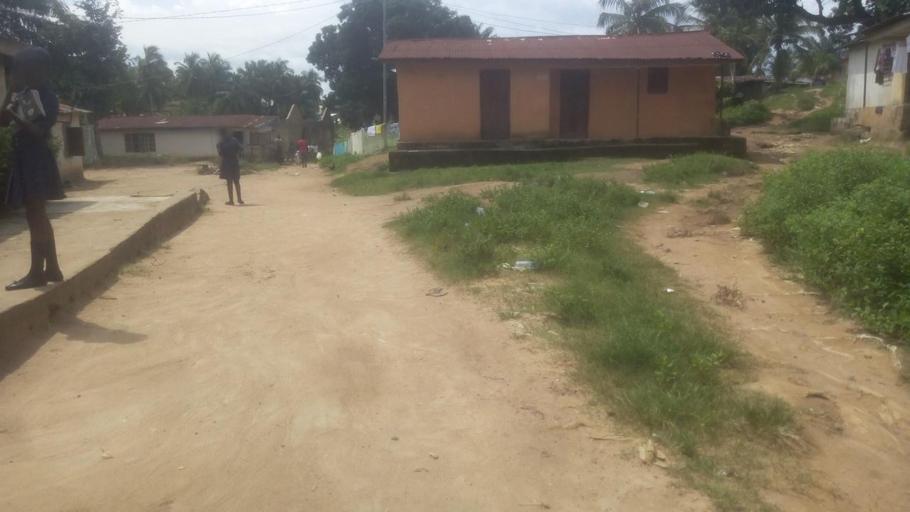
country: SL
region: Western Area
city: Freetown
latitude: 8.5212
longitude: -13.1501
